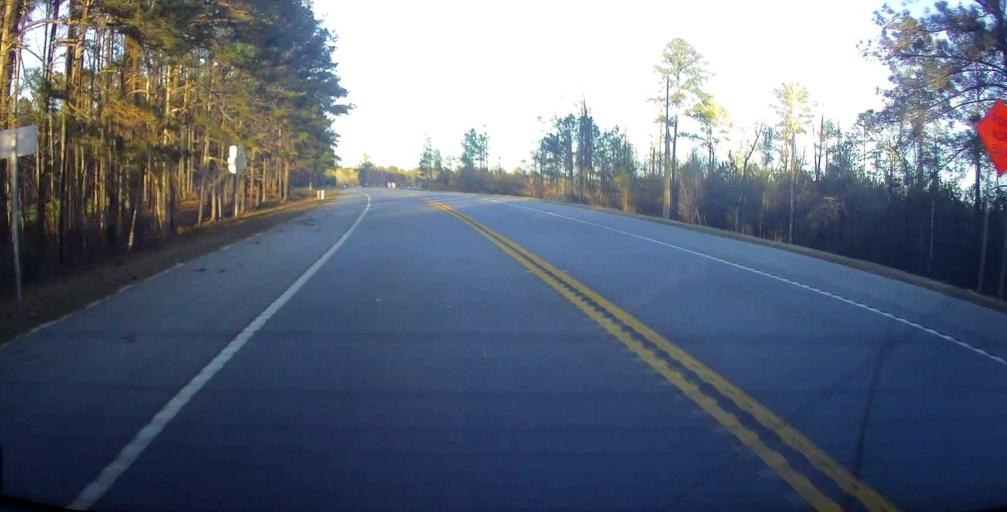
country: US
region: Georgia
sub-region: Harris County
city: Hamilton
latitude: 32.6638
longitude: -84.9778
